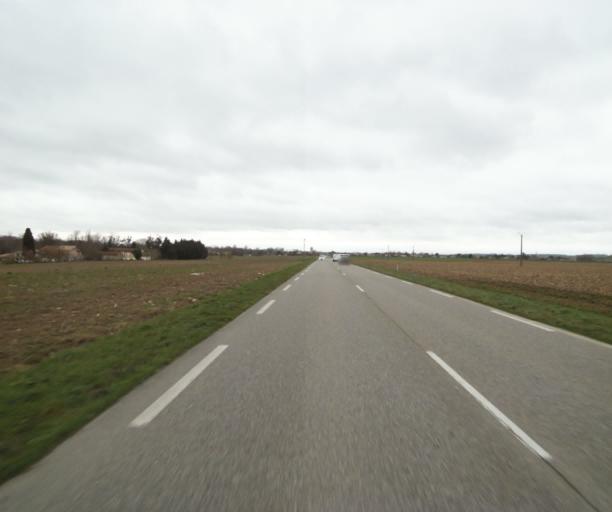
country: FR
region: Midi-Pyrenees
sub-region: Departement de l'Ariege
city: Pamiers
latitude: 43.1767
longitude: 1.6063
